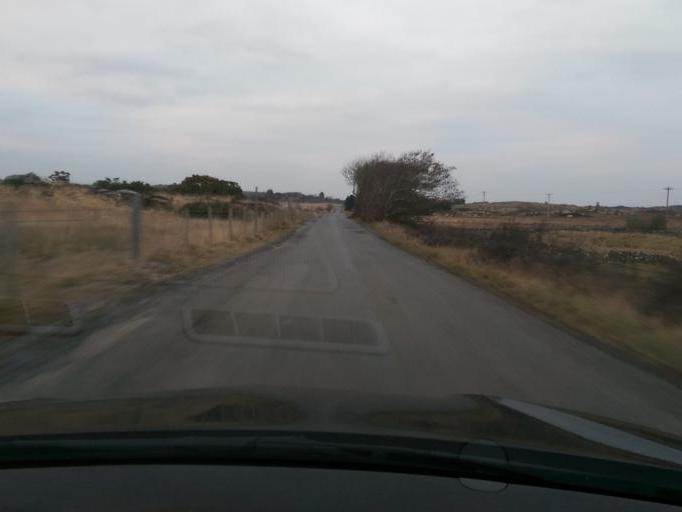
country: IE
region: Connaught
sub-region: County Galway
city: Bearna
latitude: 53.2853
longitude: -9.1634
